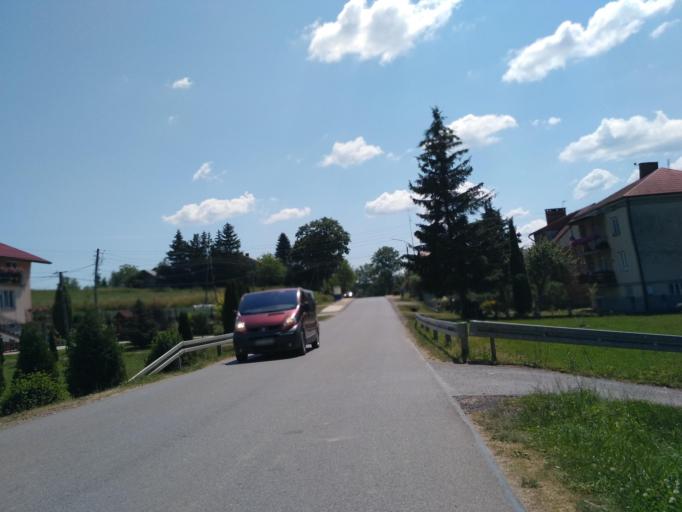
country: PL
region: Subcarpathian Voivodeship
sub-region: Powiat sanocki
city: Niebieszczany
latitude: 49.4993
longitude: 22.1635
